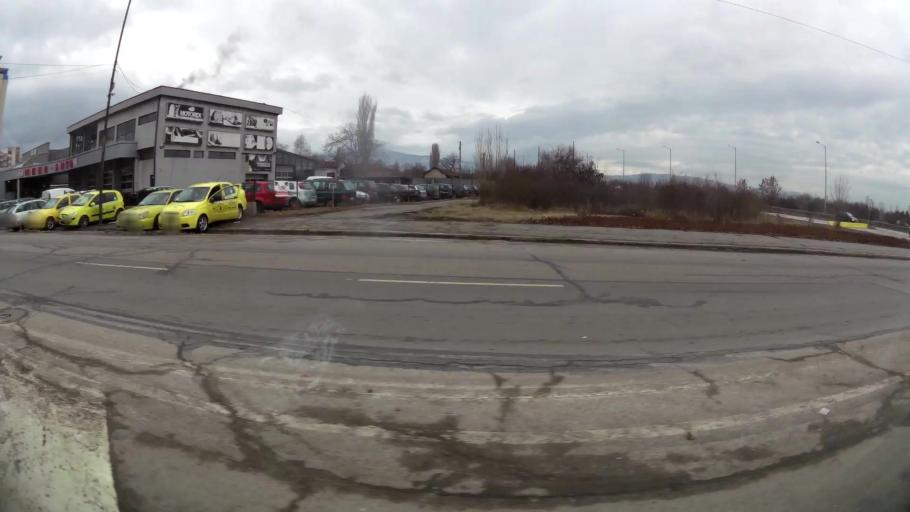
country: BG
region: Sofia-Capital
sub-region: Stolichna Obshtina
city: Sofia
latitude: 42.7322
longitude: 23.2843
